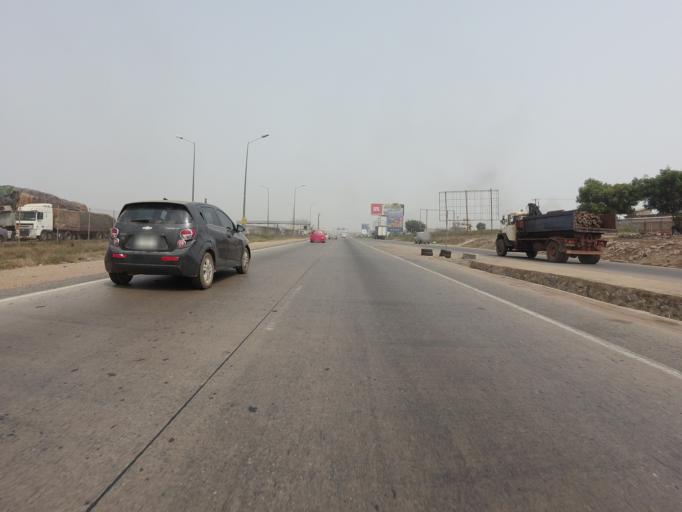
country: GH
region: Greater Accra
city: Tema
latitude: 5.6828
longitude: -0.0242
